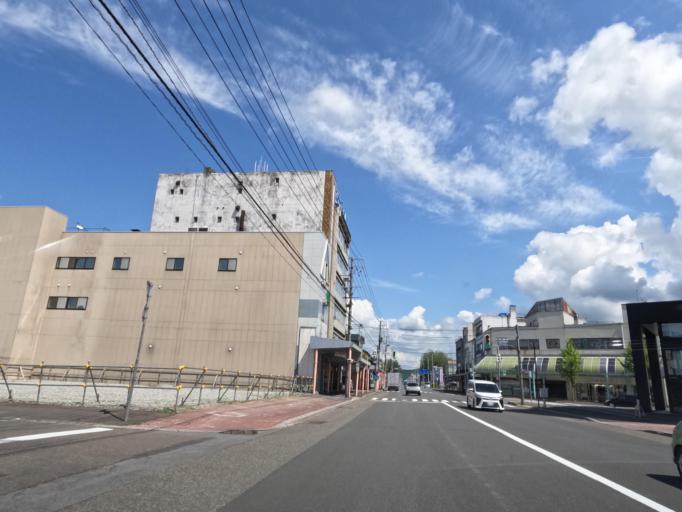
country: JP
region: Hokkaido
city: Takikawa
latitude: 43.5582
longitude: 141.9069
